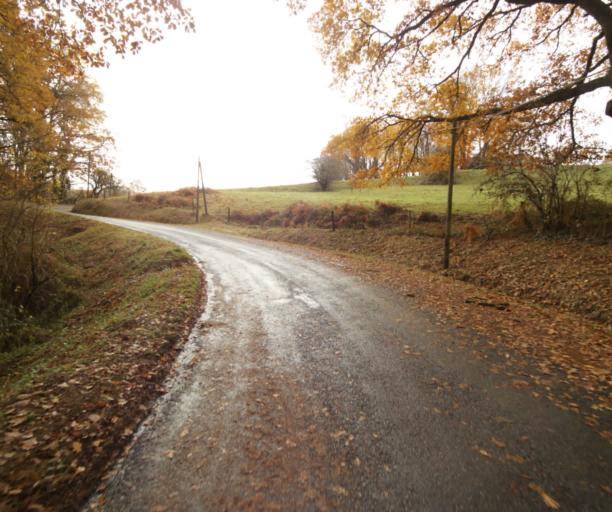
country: FR
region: Limousin
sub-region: Departement de la Correze
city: Sainte-Fereole
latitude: 45.2092
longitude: 1.6297
